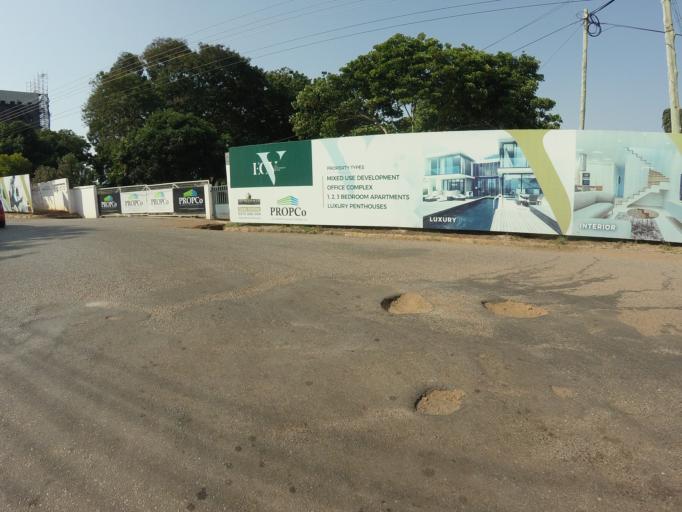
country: GH
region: Greater Accra
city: Accra
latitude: 5.5779
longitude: -0.1600
